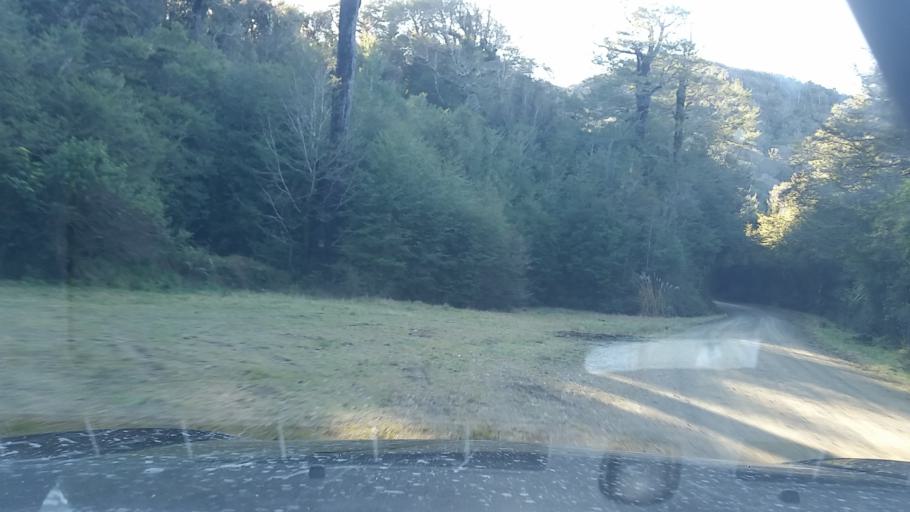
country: NZ
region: Marlborough
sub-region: Marlborough District
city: Picton
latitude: -41.0712
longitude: 174.1571
